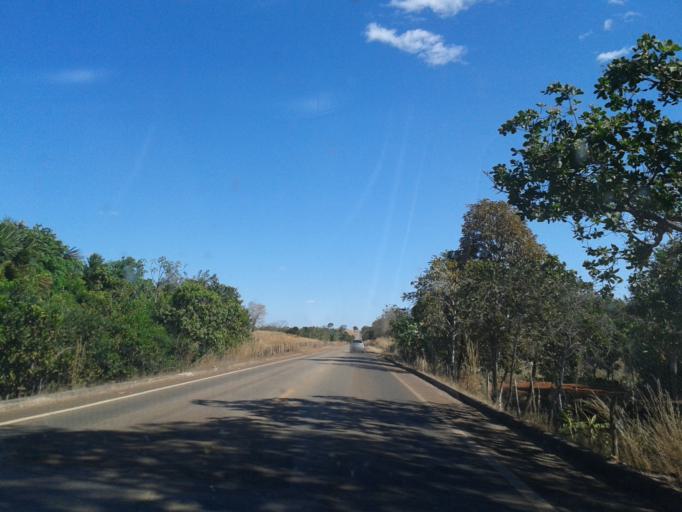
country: BR
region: Goias
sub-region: Crixas
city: Crixas
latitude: -14.1289
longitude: -50.3507
